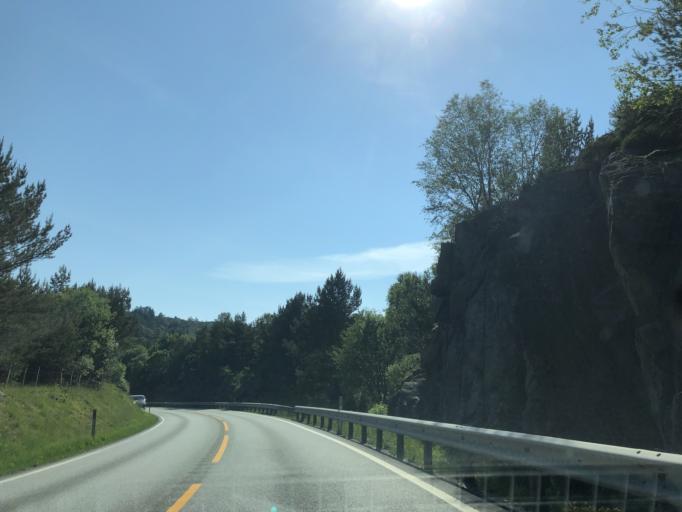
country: NO
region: Rogaland
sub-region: Tysvaer
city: Tysvaer
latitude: 59.3585
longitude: 5.4528
